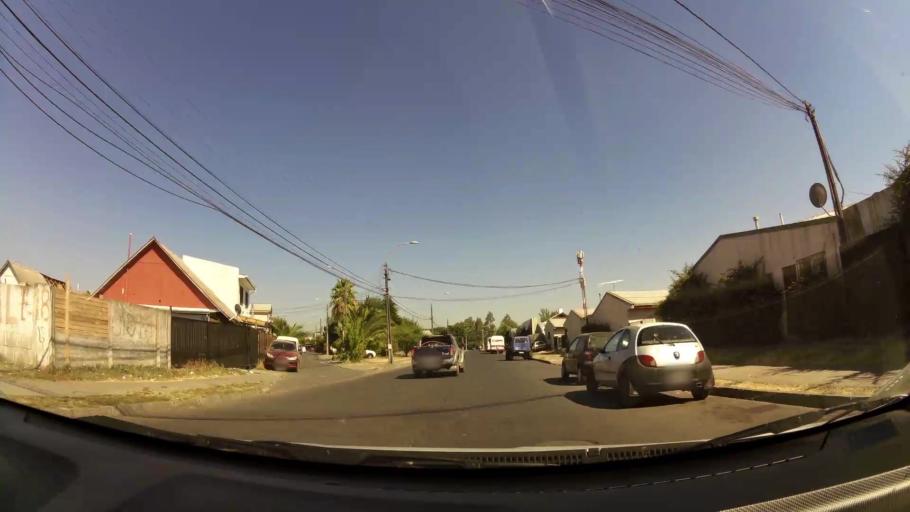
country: CL
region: Maule
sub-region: Provincia de Curico
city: Curico
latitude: -34.9767
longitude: -71.2556
